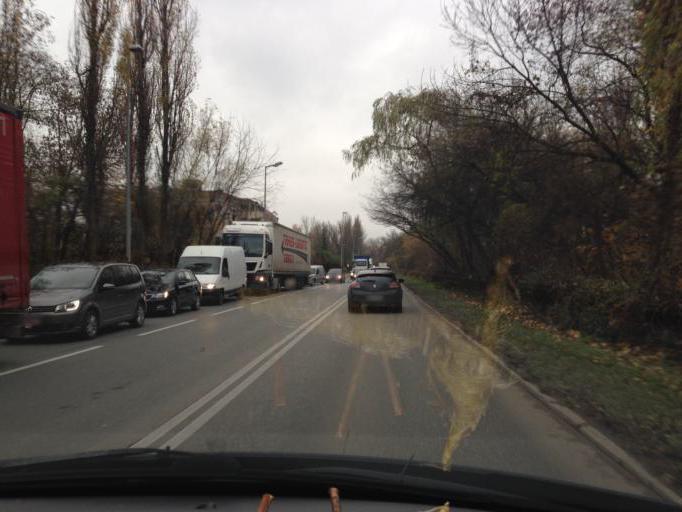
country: PL
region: Lesser Poland Voivodeship
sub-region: Powiat wielicki
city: Kokotow
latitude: 50.0770
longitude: 20.0627
